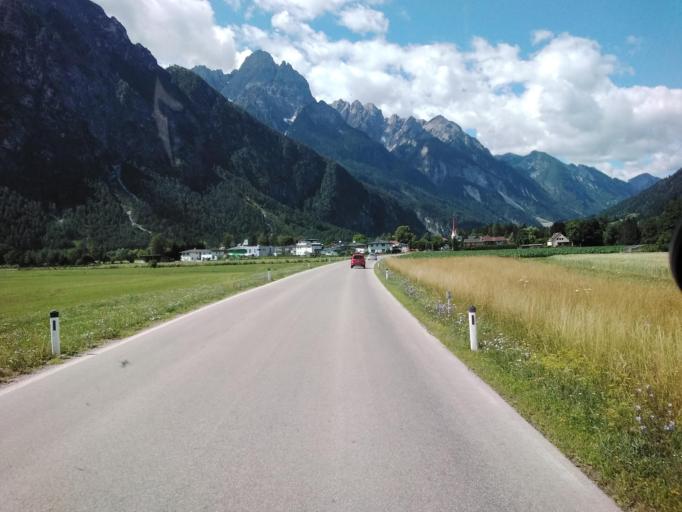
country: AT
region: Tyrol
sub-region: Politischer Bezirk Lienz
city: Amlach
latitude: 46.8179
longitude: 12.7659
